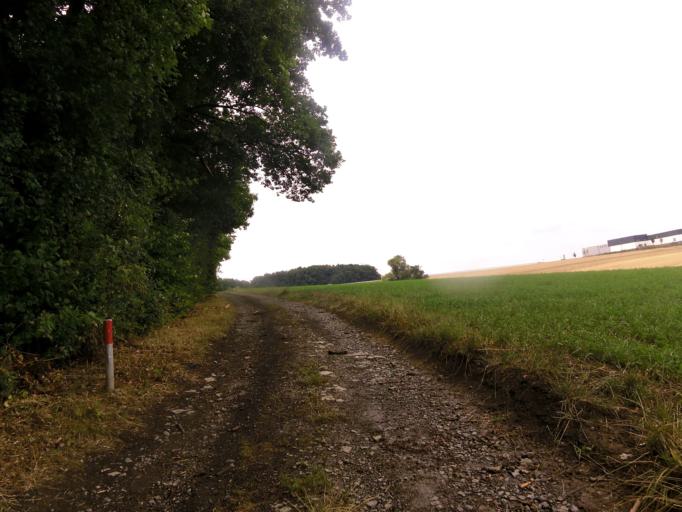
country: DE
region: Bavaria
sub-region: Regierungsbezirk Unterfranken
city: Wuerzburg
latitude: 49.7650
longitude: 9.8630
